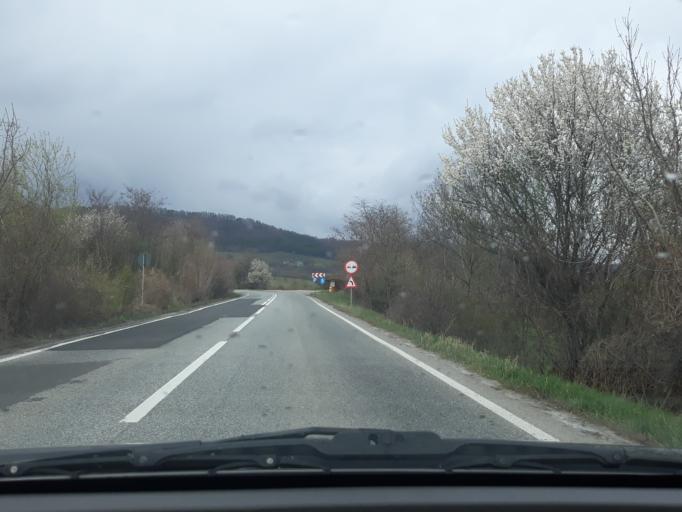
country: RO
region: Harghita
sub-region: Comuna Lupeni
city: Lupeni
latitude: 46.3992
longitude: 25.2159
